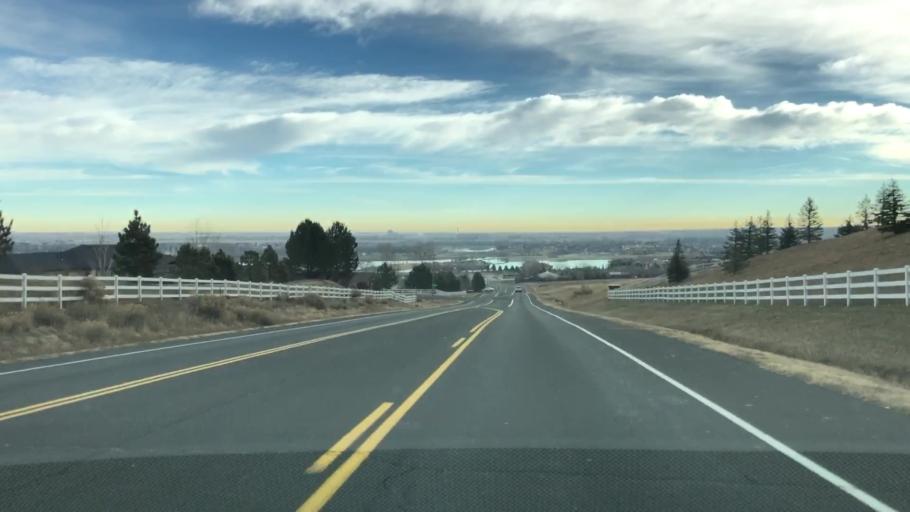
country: US
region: Colorado
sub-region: Weld County
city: Windsor
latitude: 40.4507
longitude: -104.9207
